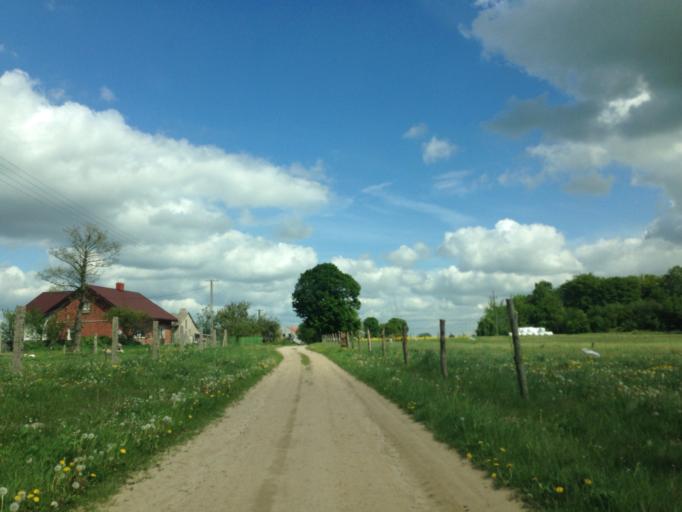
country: PL
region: Warmian-Masurian Voivodeship
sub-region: Powiat ostrodzki
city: Dabrowno
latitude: 53.3961
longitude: 20.1567
